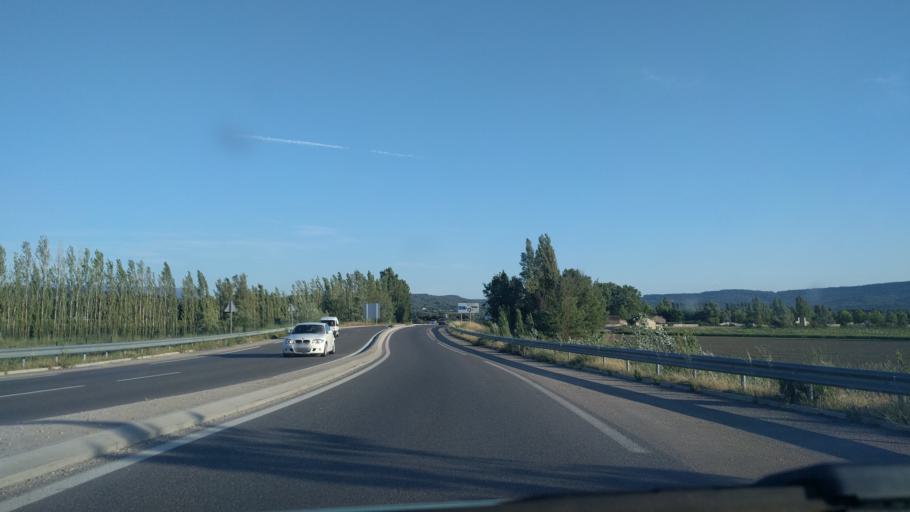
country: FR
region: Provence-Alpes-Cote d'Azur
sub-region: Departement du Vaucluse
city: Pertuis
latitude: 43.6625
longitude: 5.4946
